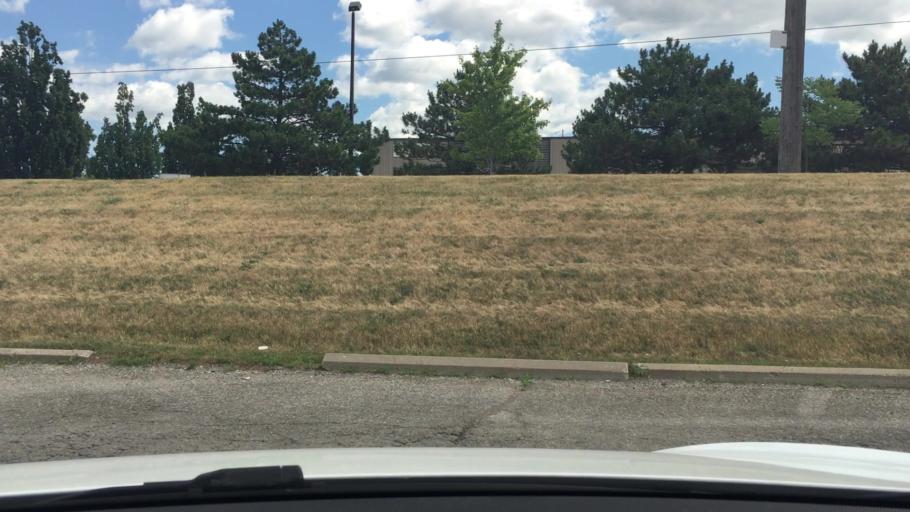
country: CA
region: Ontario
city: Scarborough
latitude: 43.7950
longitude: -79.2506
